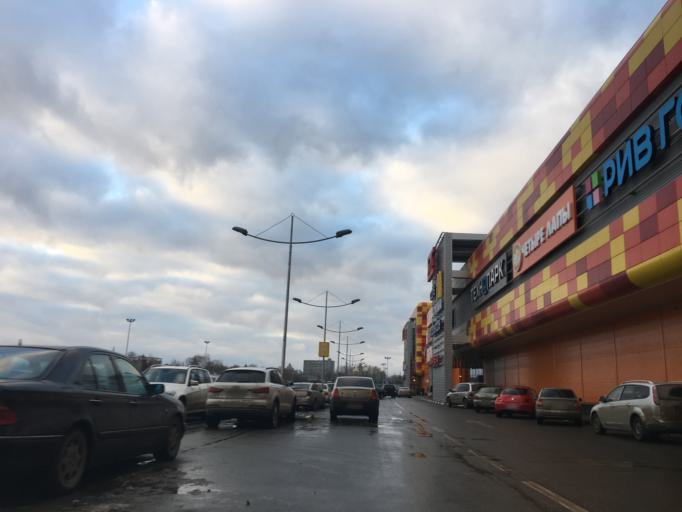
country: RU
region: Tula
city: Tula
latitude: 54.1928
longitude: 37.6380
